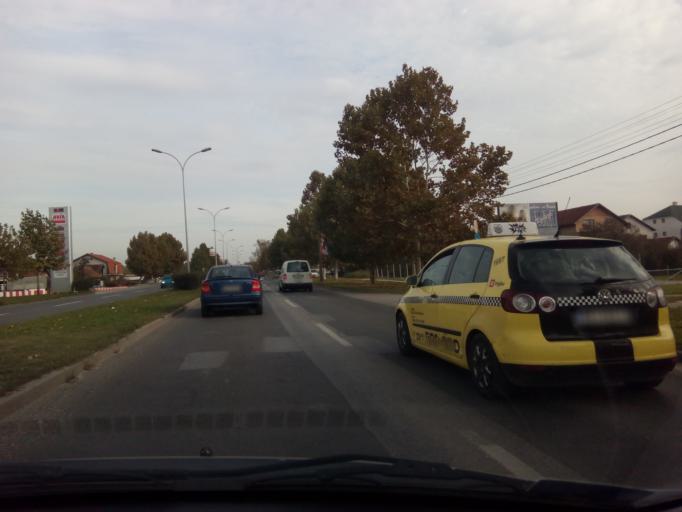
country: RS
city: Veternik
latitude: 45.2435
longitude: 19.7854
